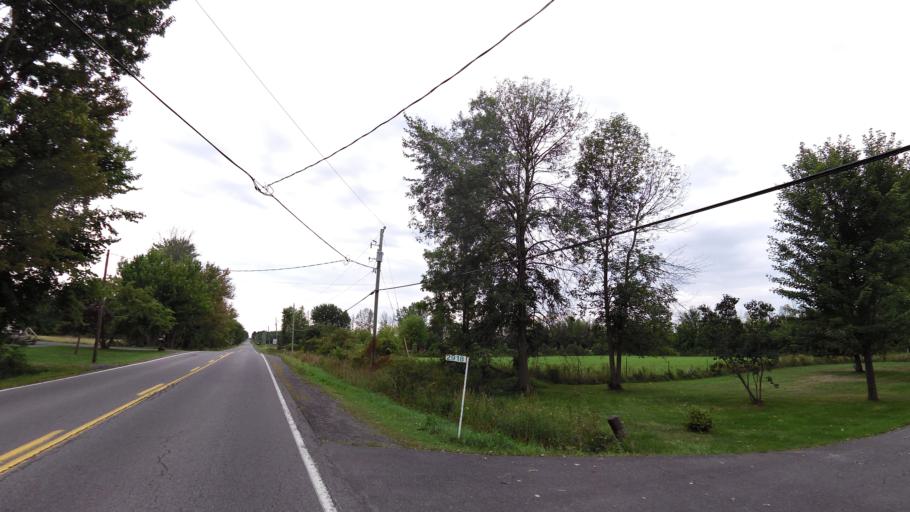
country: CA
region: Ontario
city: Ottawa
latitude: 45.2238
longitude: -75.4666
